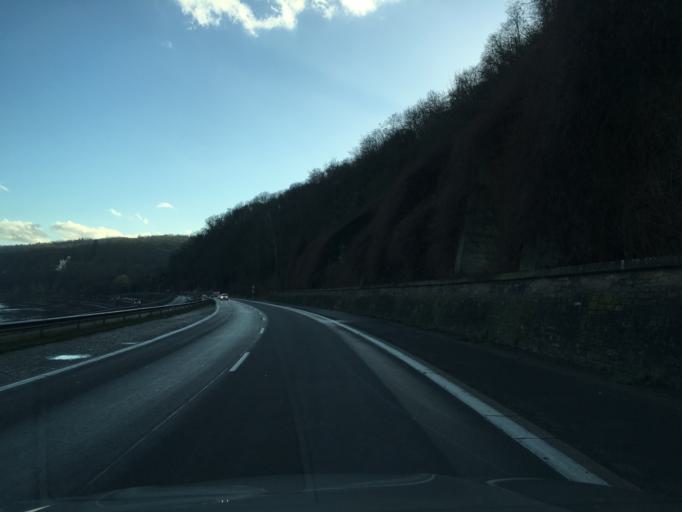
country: DE
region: Rheinland-Pfalz
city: Unkel
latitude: 50.5966
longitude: 7.2073
